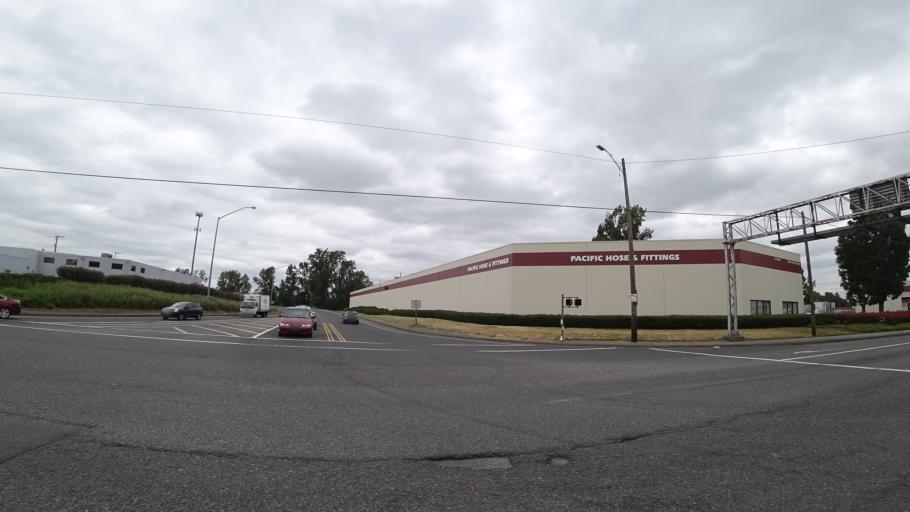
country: US
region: Washington
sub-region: Clark County
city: Vancouver
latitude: 45.5840
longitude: -122.6755
